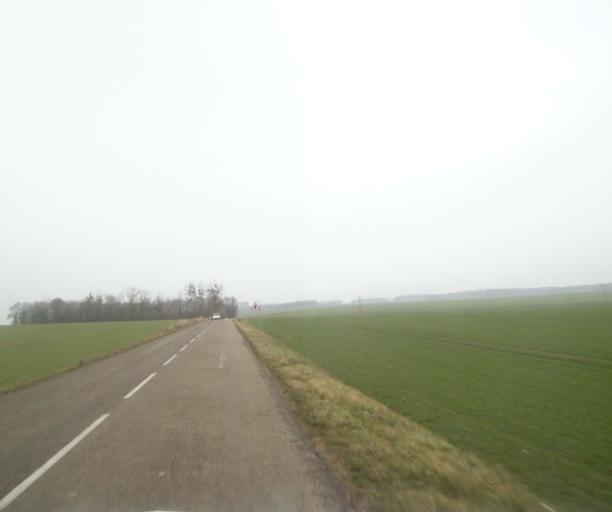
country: FR
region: Champagne-Ardenne
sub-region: Departement de la Haute-Marne
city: Bienville
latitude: 48.5217
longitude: 5.0377
